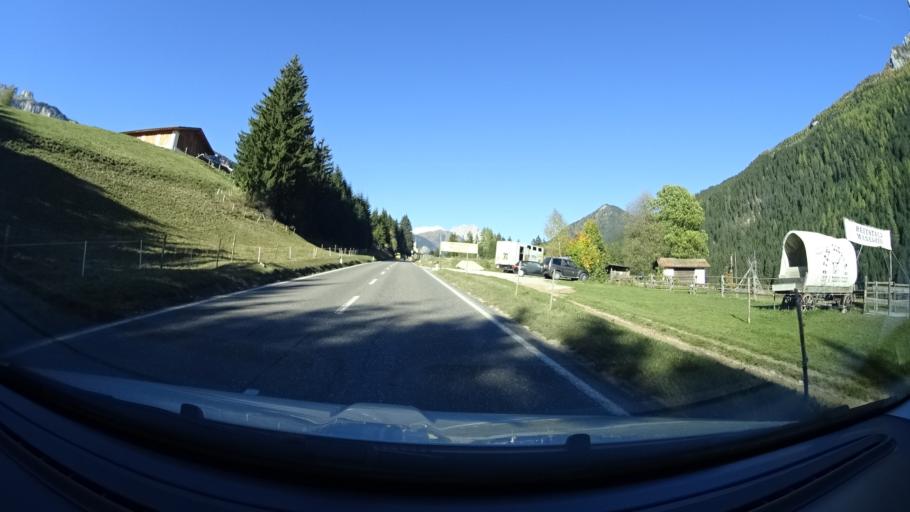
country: IT
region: Trentino-Alto Adige
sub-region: Provincia di Trento
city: Vigo di Fassa
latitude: 46.4124
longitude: 11.6776
